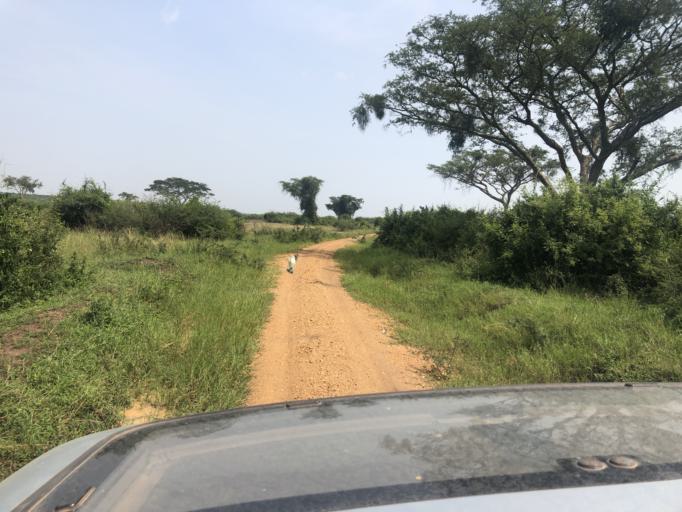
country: UG
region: Western Region
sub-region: Rubirizi District
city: Rubirizi
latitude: -0.2126
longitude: 29.9548
